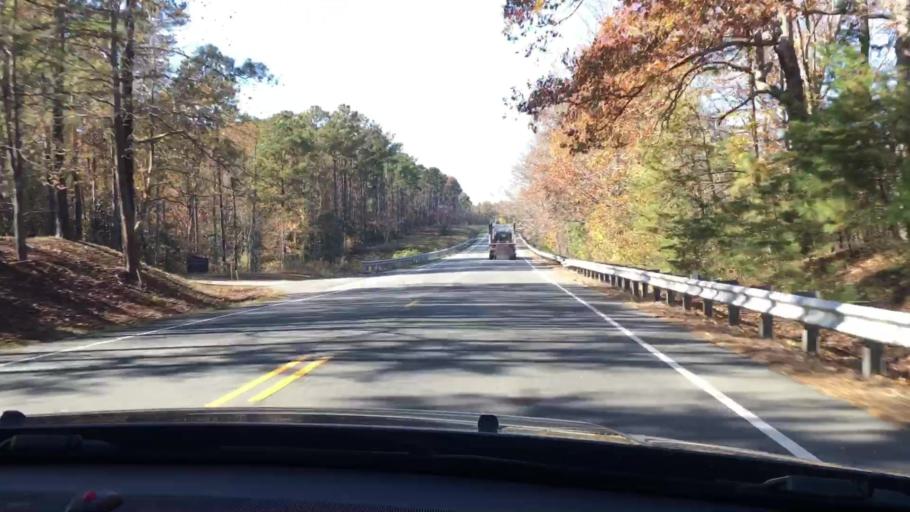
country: US
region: Virginia
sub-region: King William County
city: Central Garage
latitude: 37.7867
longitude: -77.1756
